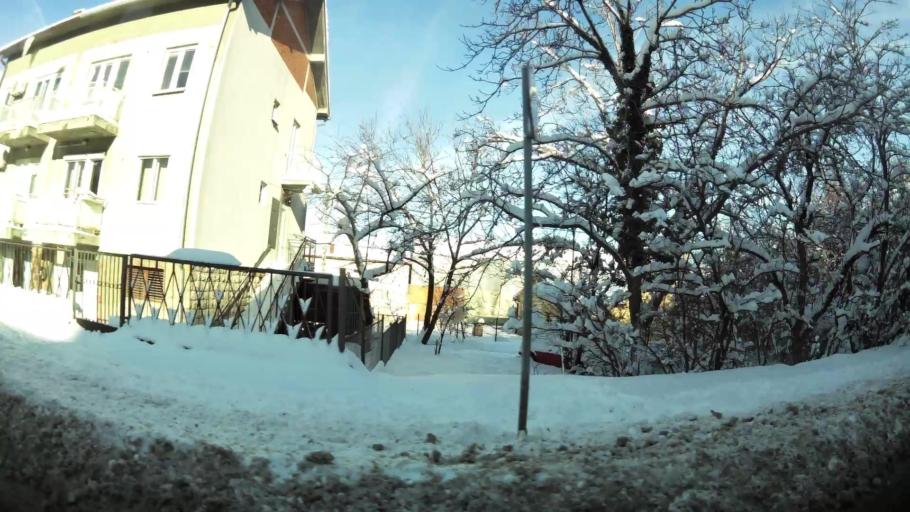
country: RS
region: Central Serbia
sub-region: Belgrade
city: Zvezdara
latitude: 44.7860
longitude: 20.5124
